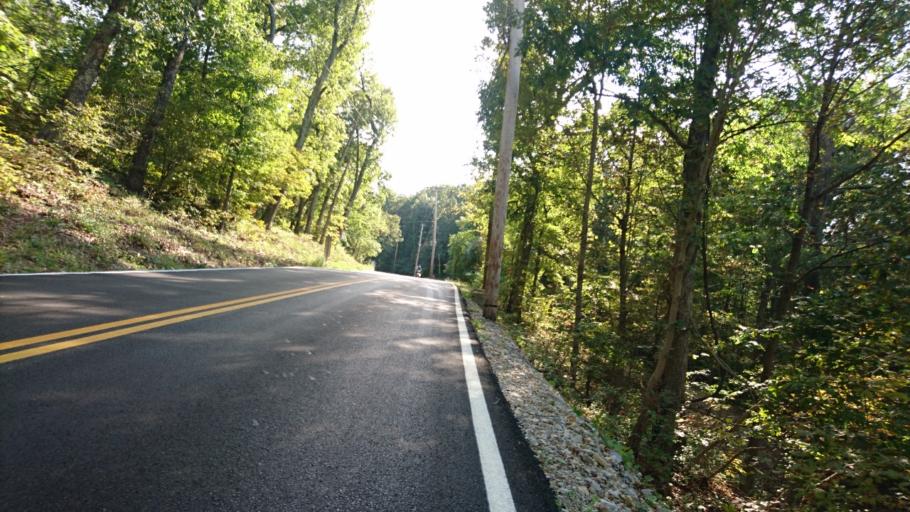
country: US
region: Missouri
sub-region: Saint Louis County
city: Eureka
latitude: 38.5298
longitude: -90.6419
